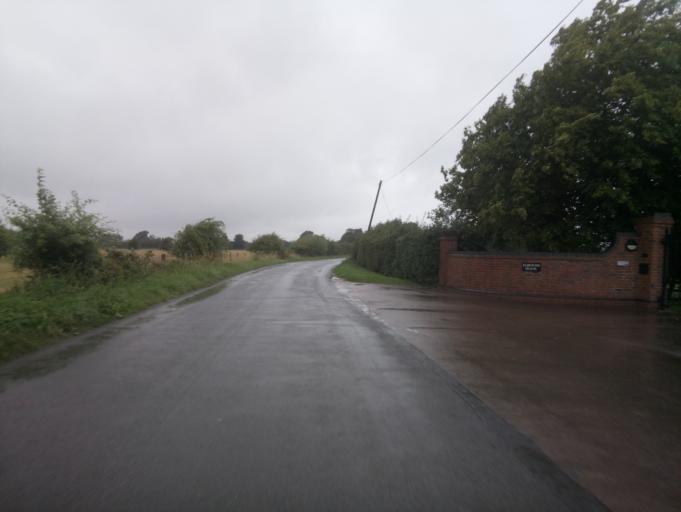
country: GB
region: England
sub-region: Gloucestershire
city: Uckington
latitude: 51.9362
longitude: -2.1250
